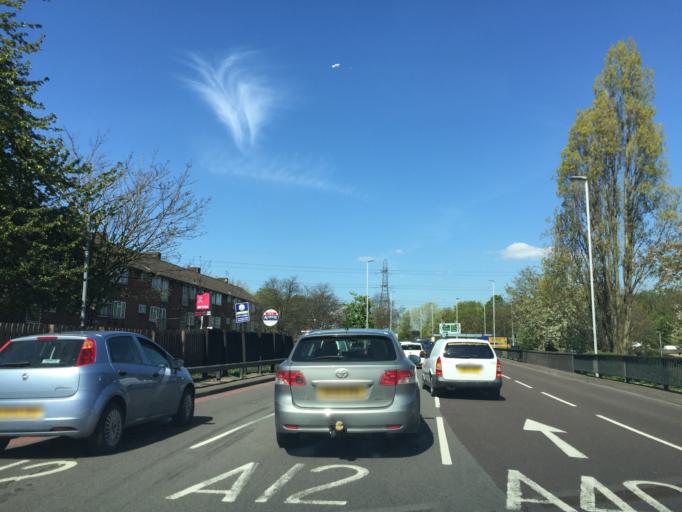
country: GB
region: England
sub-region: Greater London
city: Ilford
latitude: 51.5753
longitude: 0.0443
